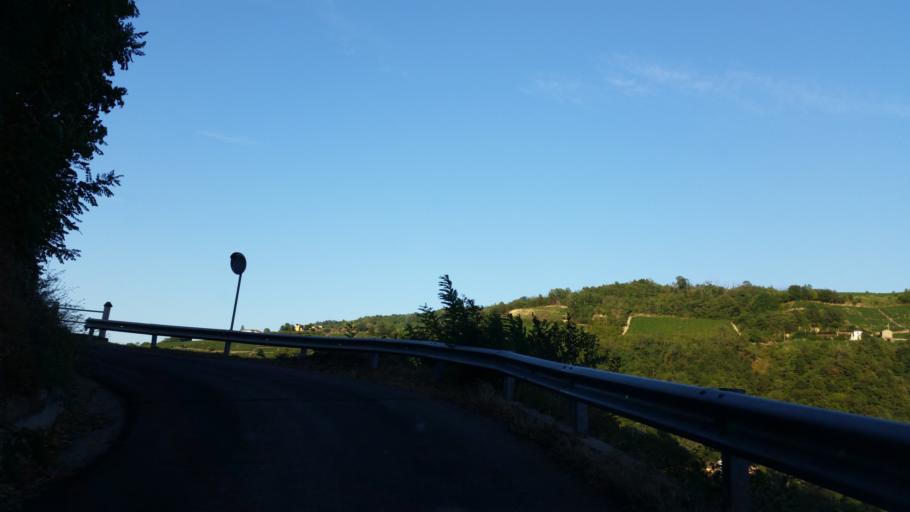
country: IT
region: Piedmont
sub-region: Provincia di Cuneo
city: Camo
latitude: 44.6857
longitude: 8.1991
